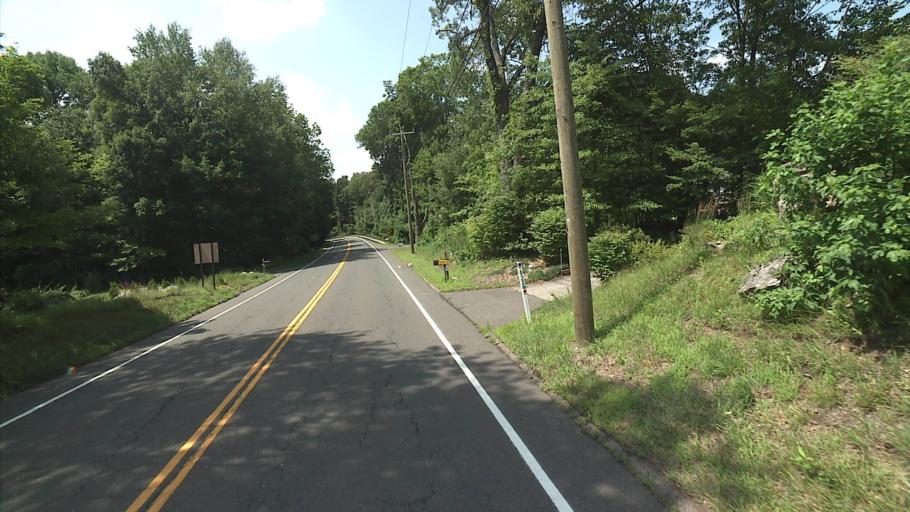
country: US
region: Connecticut
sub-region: Tolland County
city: South Coventry
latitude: 41.7827
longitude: -72.3174
